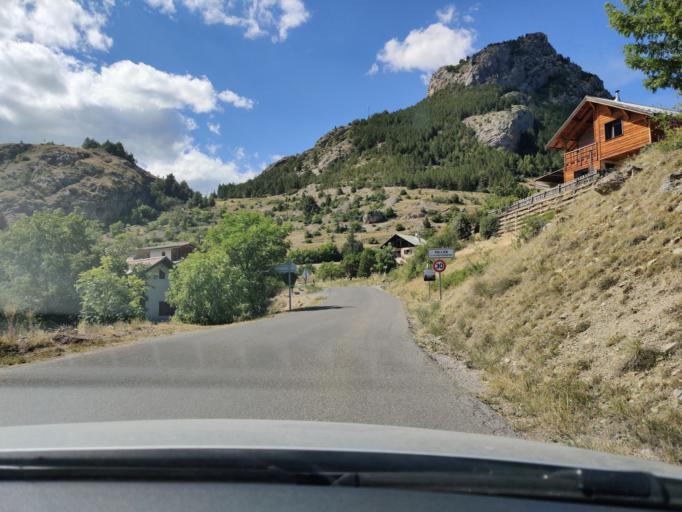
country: FR
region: Provence-Alpes-Cote d'Azur
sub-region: Departement des Hautes-Alpes
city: Saint-Martin-de-Queyrieres
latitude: 44.7393
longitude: 6.5700
